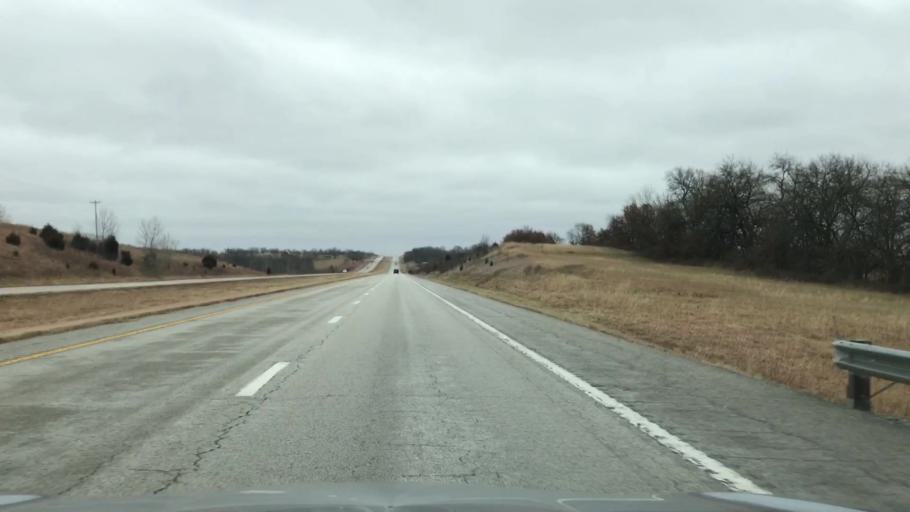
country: US
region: Missouri
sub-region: Clinton County
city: Cameron
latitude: 39.7506
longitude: -94.1268
